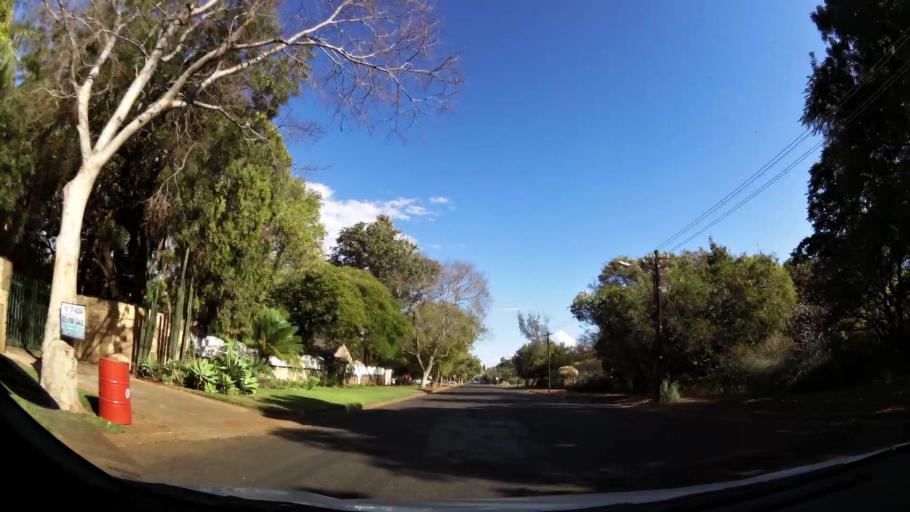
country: ZA
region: Limpopo
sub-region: Waterberg District Municipality
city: Mokopane
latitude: -24.1840
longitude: 28.9993
